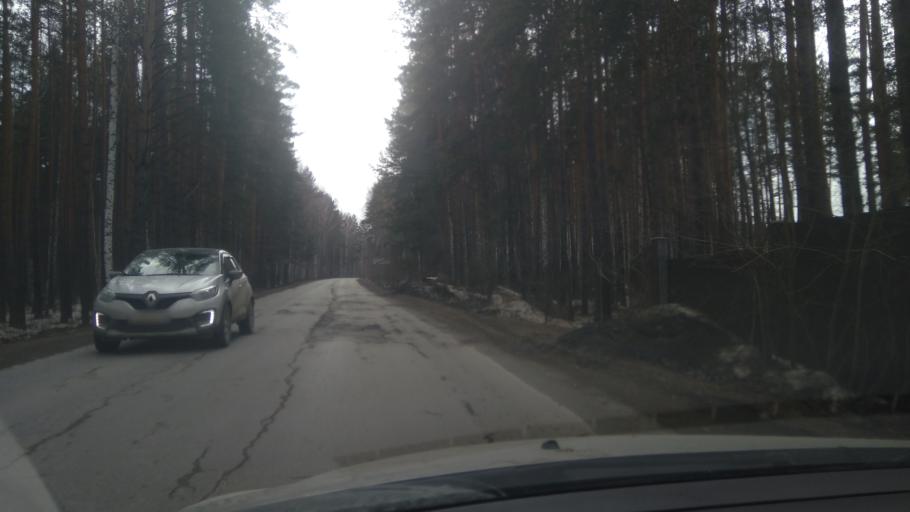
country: RU
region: Sverdlovsk
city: Severka
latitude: 56.8397
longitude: 60.3846
